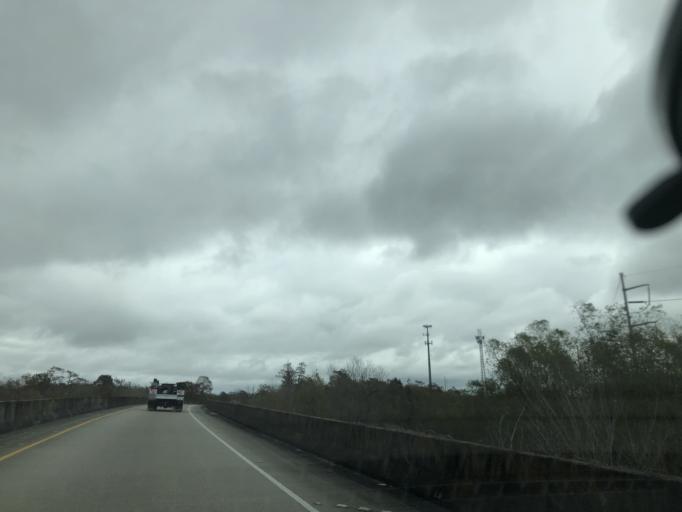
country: US
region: Louisiana
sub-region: Saint Charles Parish
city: Saint Rose
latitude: 29.9734
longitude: -90.3199
